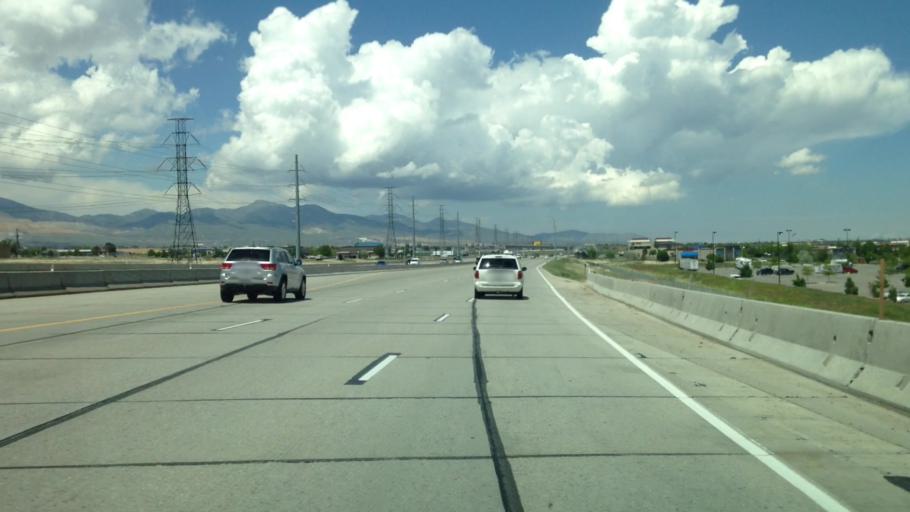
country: US
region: Utah
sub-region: Salt Lake County
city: Bluffdale
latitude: 40.5036
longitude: -111.9784
